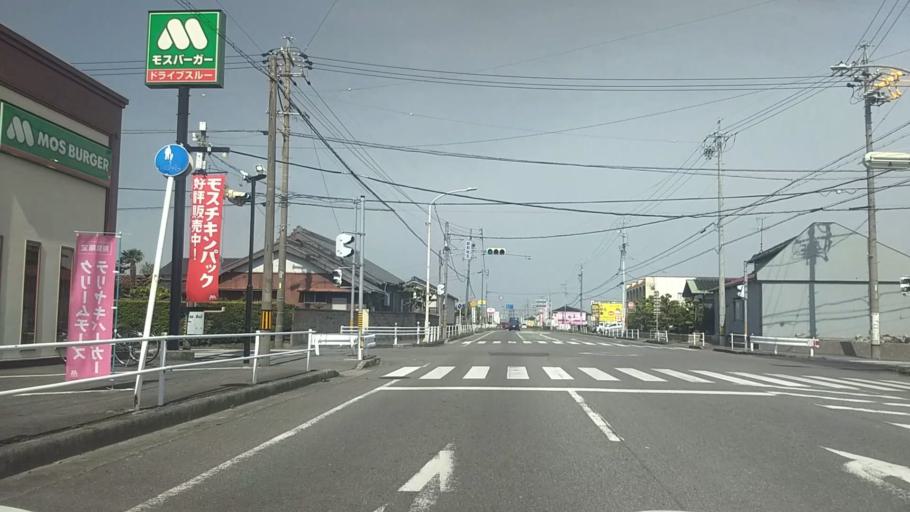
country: JP
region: Aichi
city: Anjo
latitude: 34.9450
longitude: 137.1202
